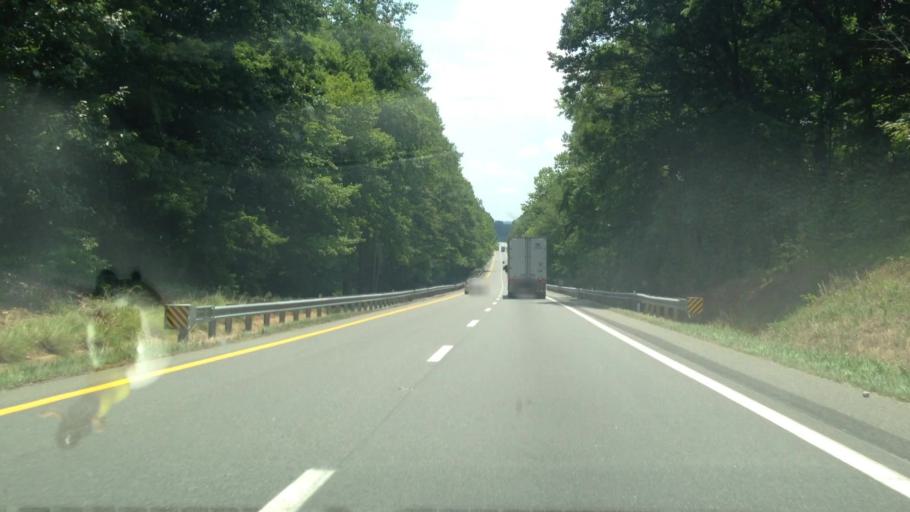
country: US
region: Virginia
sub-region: City of Martinsville
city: Martinsville
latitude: 36.6355
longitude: -79.8903
